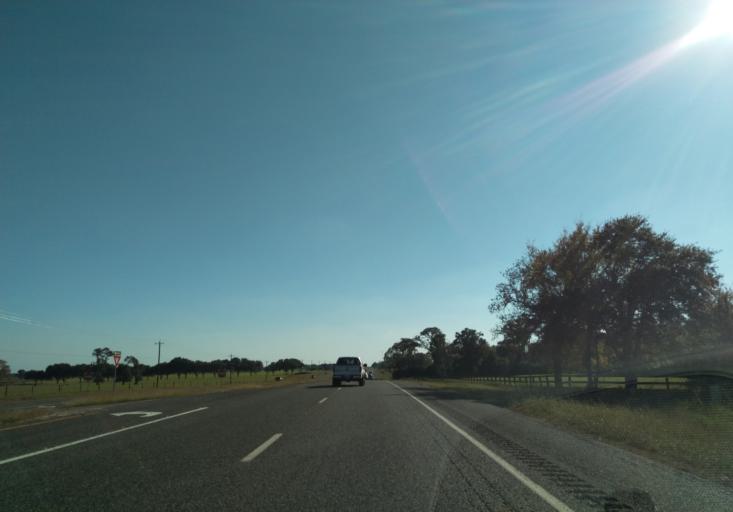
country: US
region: Texas
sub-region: Waller County
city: Hempstead
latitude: 30.1569
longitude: -96.0686
